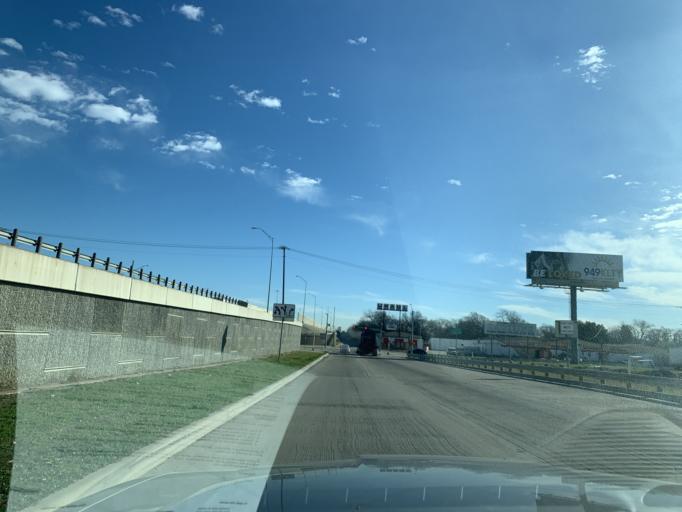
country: US
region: Texas
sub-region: Dallas County
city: Grand Prairie
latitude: 32.7617
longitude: -96.9615
